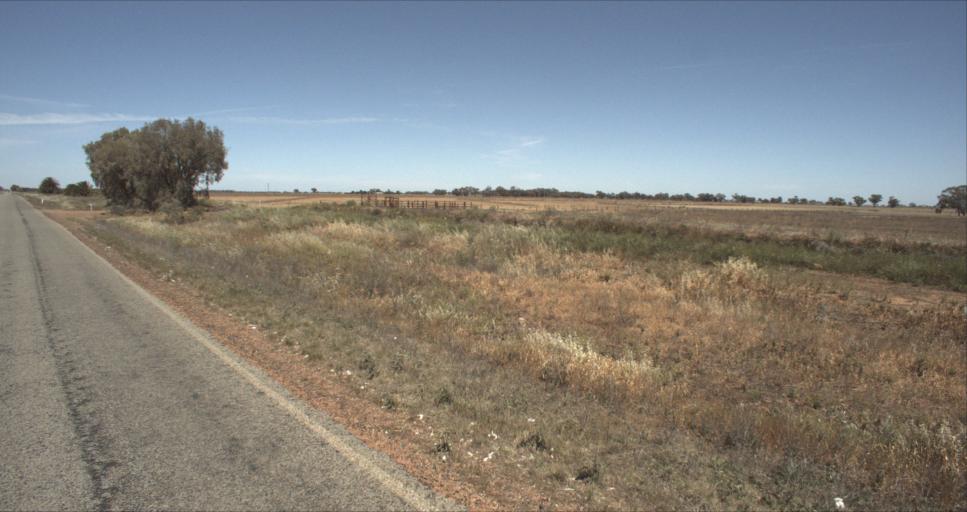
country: AU
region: New South Wales
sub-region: Leeton
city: Leeton
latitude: -34.4482
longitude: 146.2965
